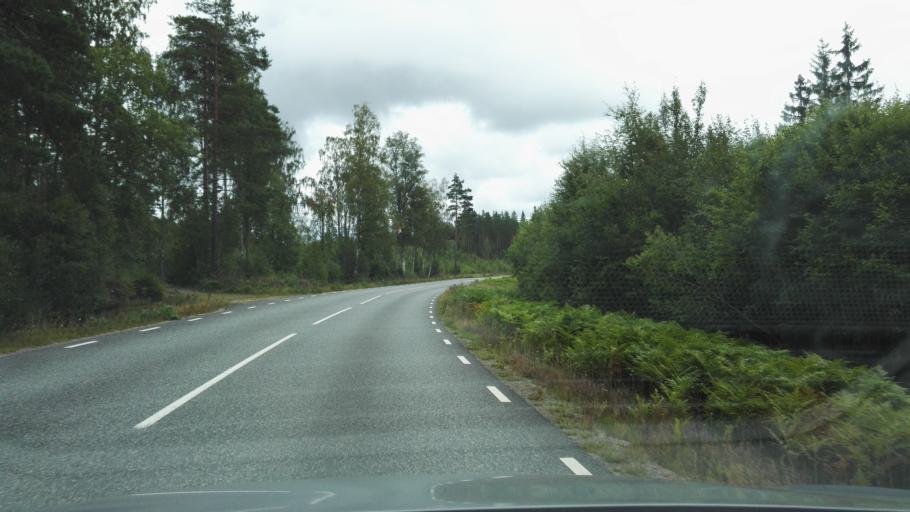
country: SE
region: Joenkoeping
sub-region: Vetlanda Kommun
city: Landsbro
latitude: 57.2776
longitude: 14.9017
